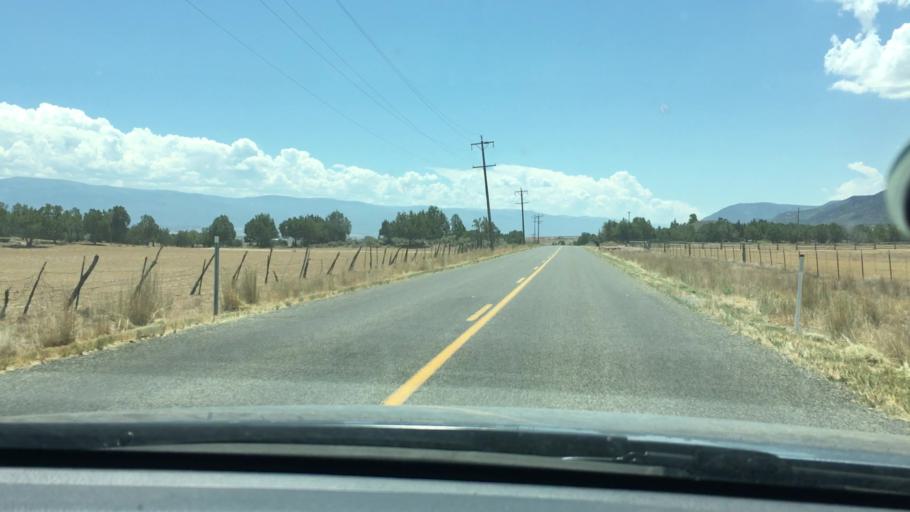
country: US
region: Utah
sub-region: Sanpete County
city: Fountain Green
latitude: 39.5934
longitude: -111.6428
